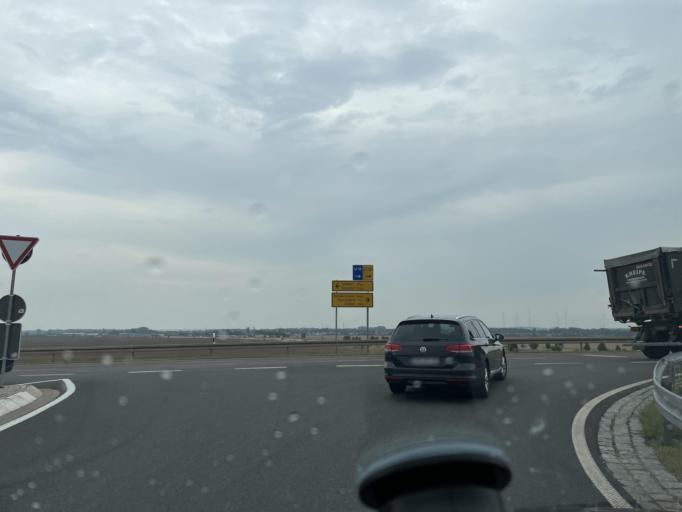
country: DE
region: Saxony-Anhalt
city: Giersleben
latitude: 51.7885
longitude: 11.5693
